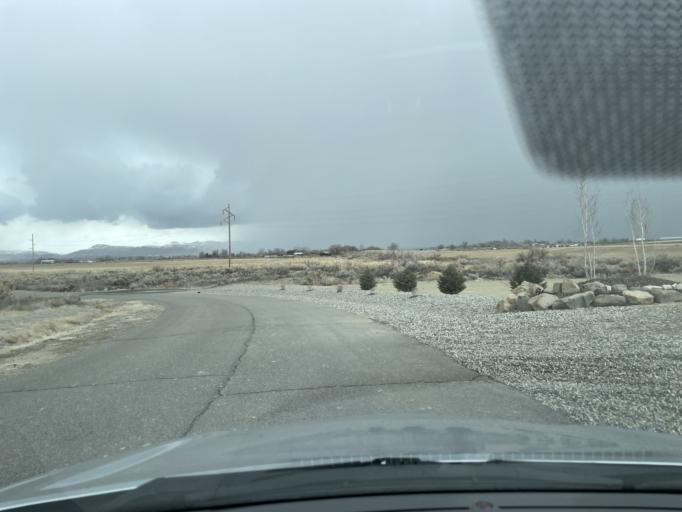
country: US
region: Colorado
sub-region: Mesa County
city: Loma
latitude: 39.2161
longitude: -108.8043
